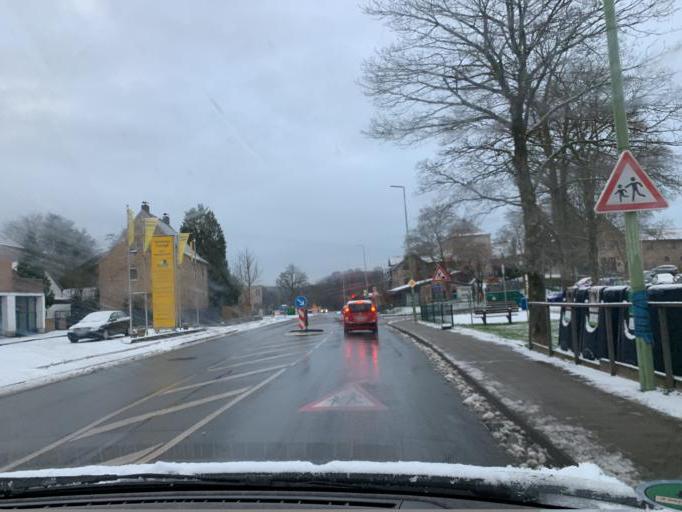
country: DE
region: North Rhine-Westphalia
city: Stolberg
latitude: 50.7563
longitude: 6.2750
